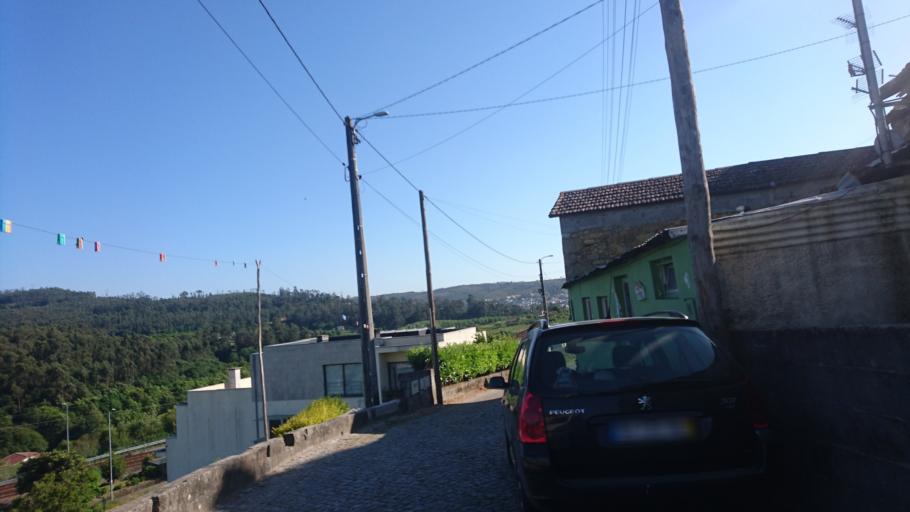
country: PT
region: Porto
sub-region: Paredes
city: Baltar
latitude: 41.1585
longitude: -8.3803
